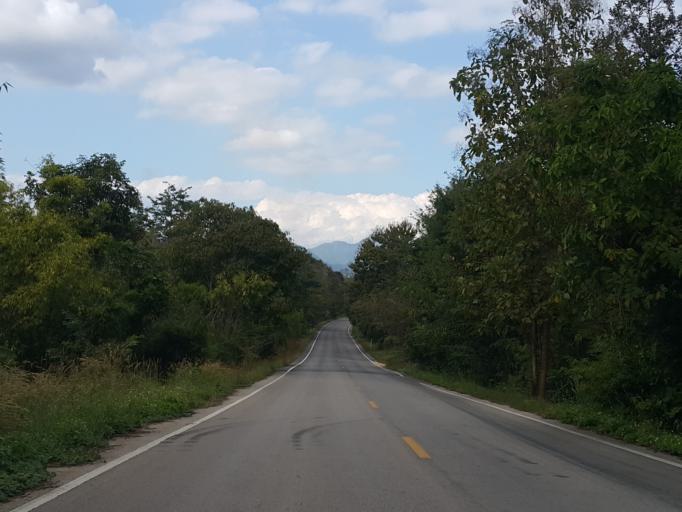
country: TH
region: Lampang
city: Chae Hom
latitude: 18.6109
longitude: 99.4832
